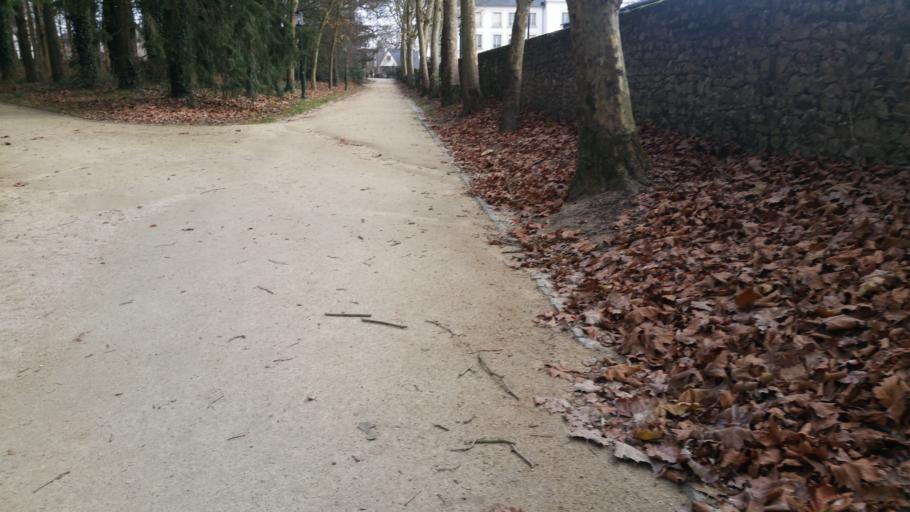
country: FR
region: Brittany
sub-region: Departement d'Ille-et-Vilaine
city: Vitre
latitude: 48.1165
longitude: -1.2068
